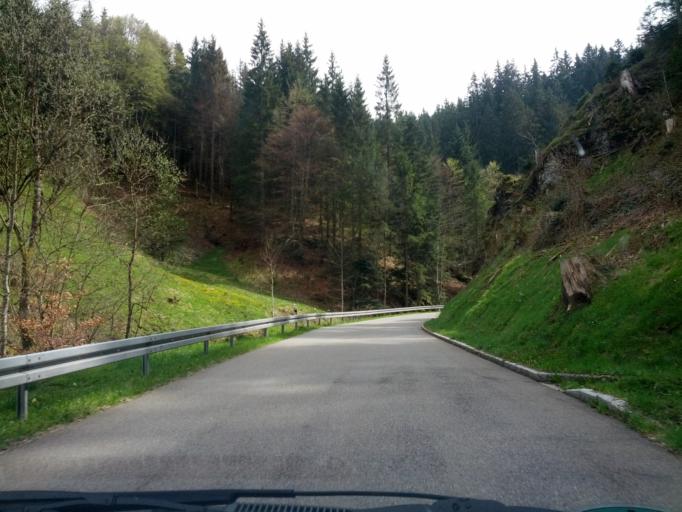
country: DE
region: Baden-Wuerttemberg
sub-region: Freiburg Region
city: Sankt Margen
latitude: 47.9962
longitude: 8.1277
